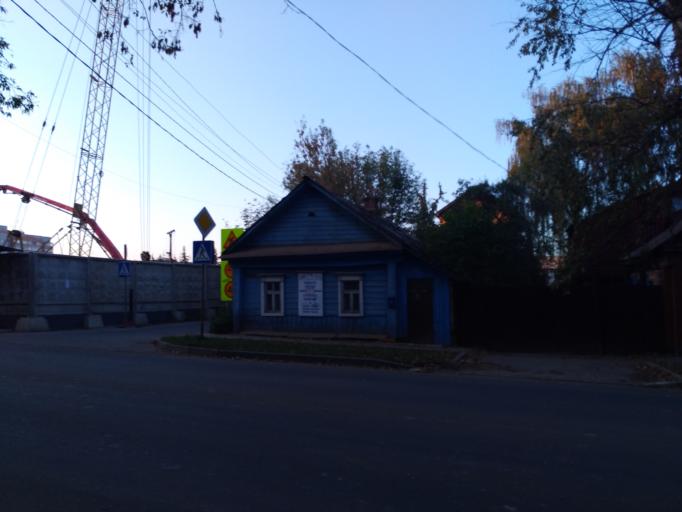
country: RU
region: Kaluga
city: Kaluga
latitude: 54.5190
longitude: 36.2709
